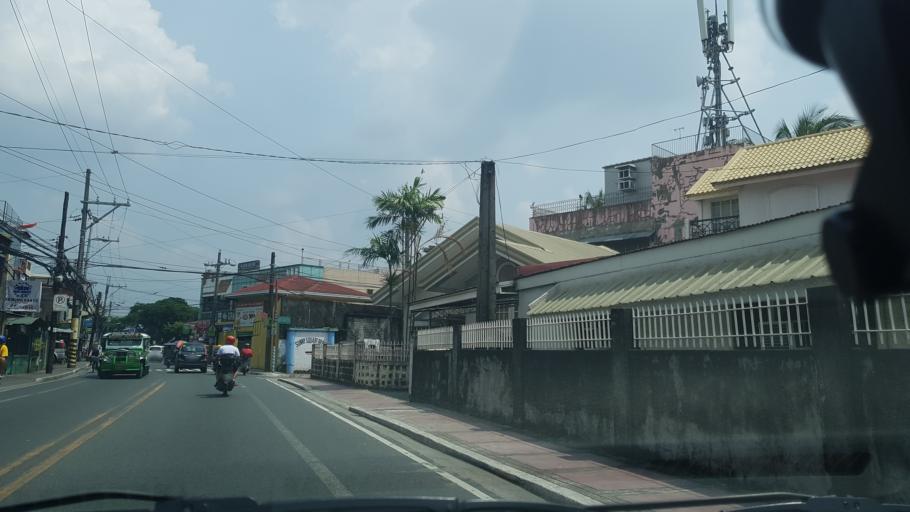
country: PH
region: Metro Manila
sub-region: Marikina
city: Calumpang
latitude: 14.6436
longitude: 121.0954
